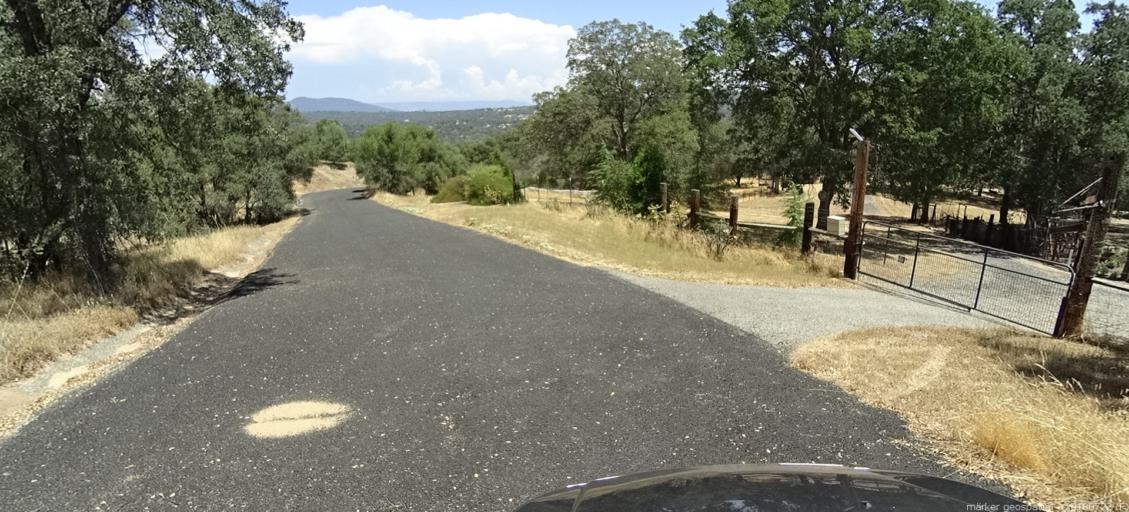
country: US
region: California
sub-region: Madera County
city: Yosemite Lakes
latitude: 37.2132
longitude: -119.7355
